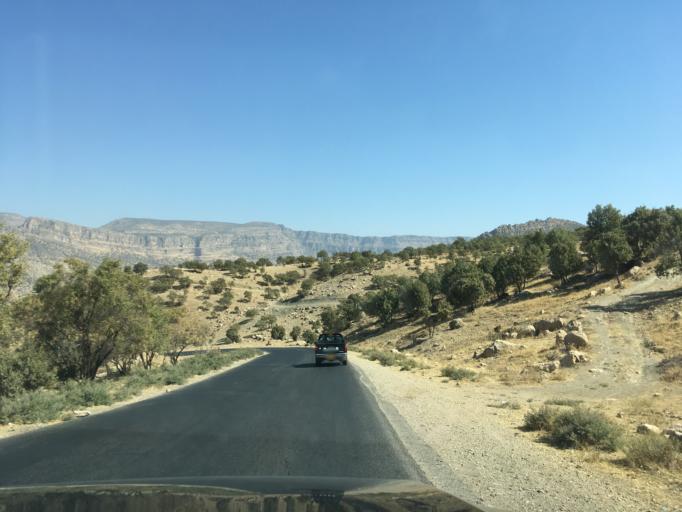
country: IQ
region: Arbil
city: Ruwandiz
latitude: 36.6493
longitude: 44.3524
